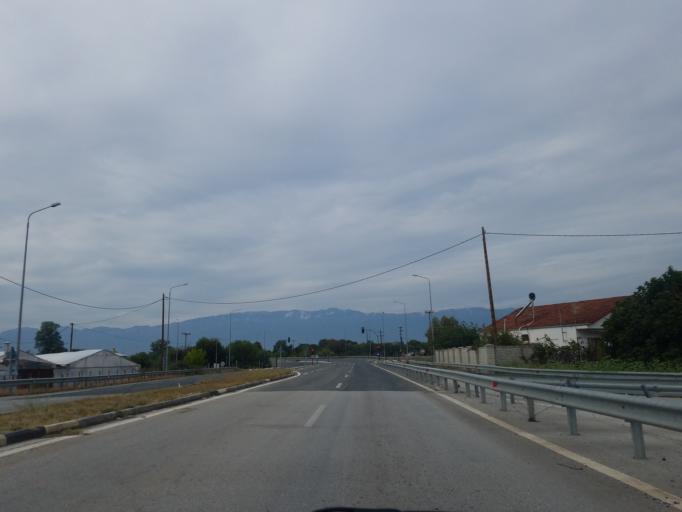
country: GR
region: Thessaly
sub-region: Trikala
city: Pyrgetos
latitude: 39.5720
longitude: 21.7452
